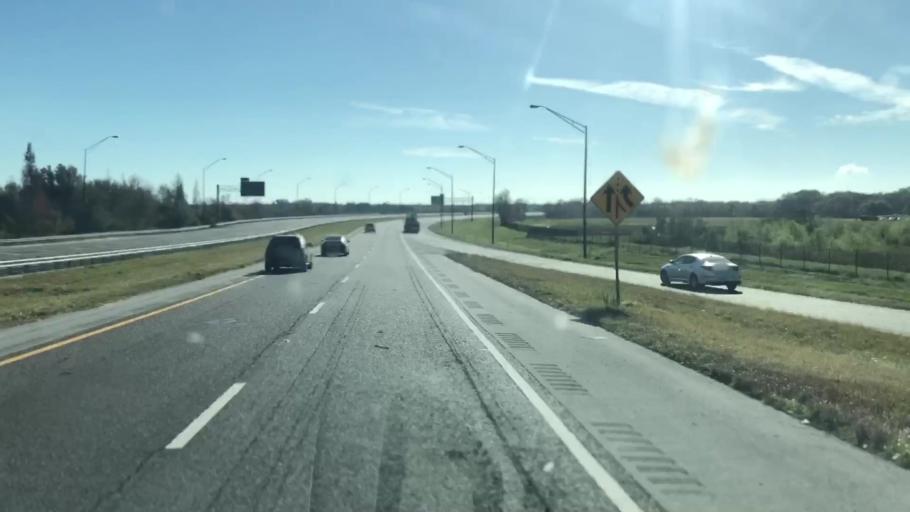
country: US
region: Florida
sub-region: Polk County
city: Winston
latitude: 28.0071
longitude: -82.0131
